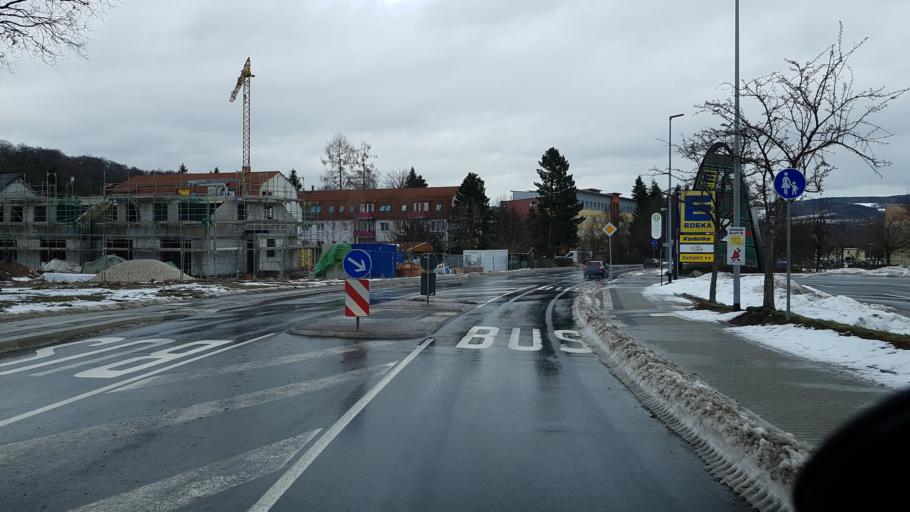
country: DE
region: Saxony
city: Kirchberg
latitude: 50.6204
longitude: 12.5108
